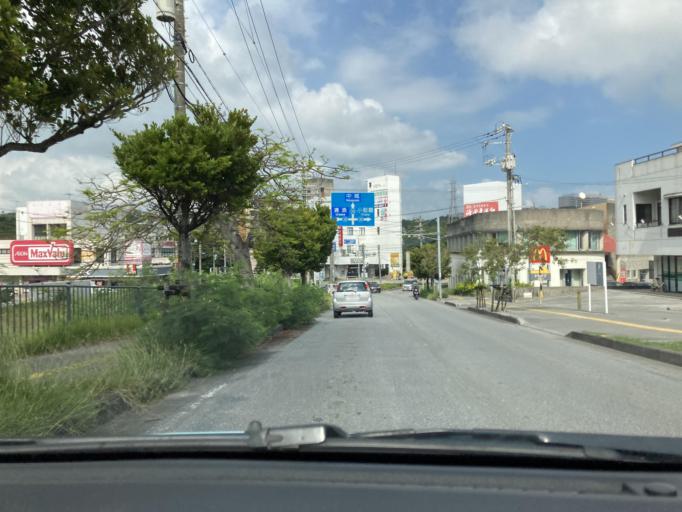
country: JP
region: Okinawa
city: Ginowan
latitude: 26.2381
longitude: 127.7483
